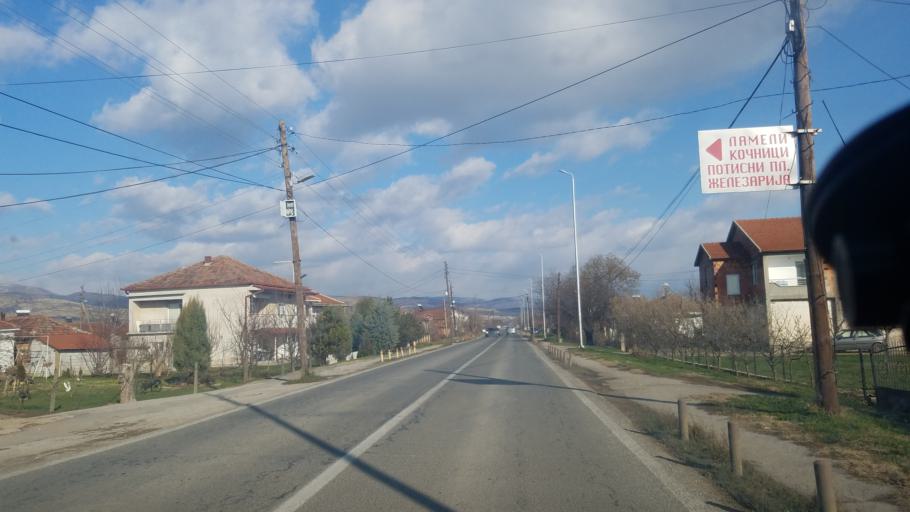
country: MK
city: Obleshevo
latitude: 41.8854
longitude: 22.3381
